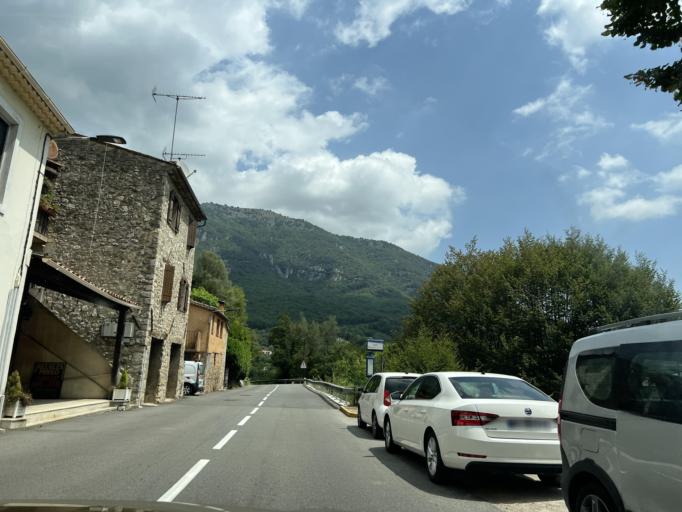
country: FR
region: Provence-Alpes-Cote d'Azur
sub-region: Departement des Alpes-Maritimes
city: Opio
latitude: 43.7132
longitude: 6.9859
